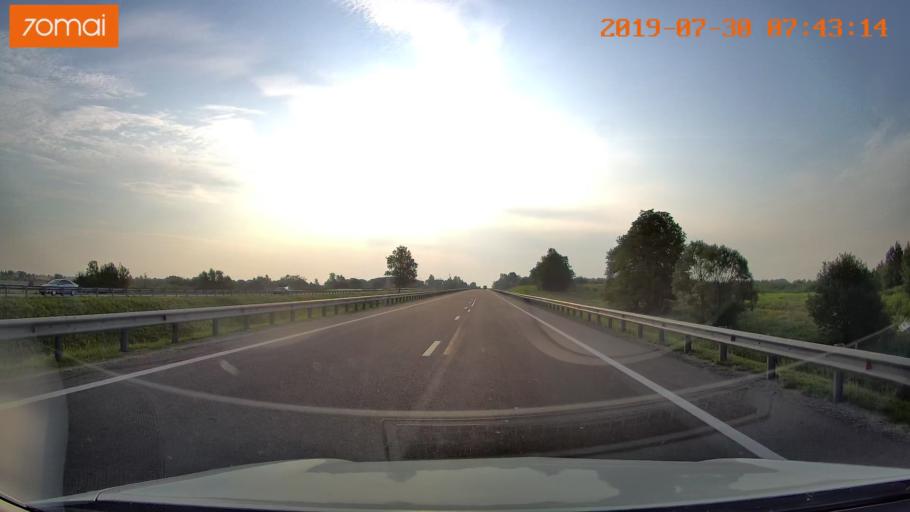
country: RU
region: Kaliningrad
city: Gvardeysk
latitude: 54.6489
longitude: 21.3010
